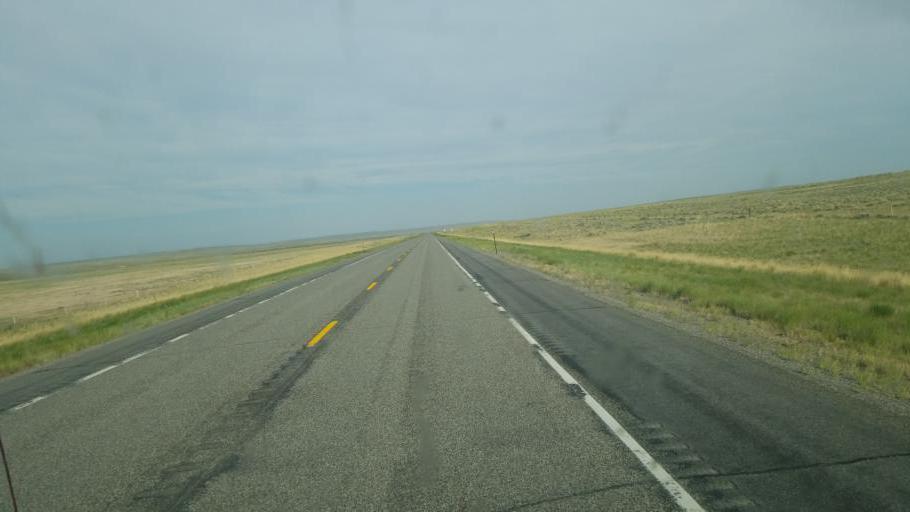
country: US
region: Wyoming
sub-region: Fremont County
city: Riverton
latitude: 43.1683
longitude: -107.8056
